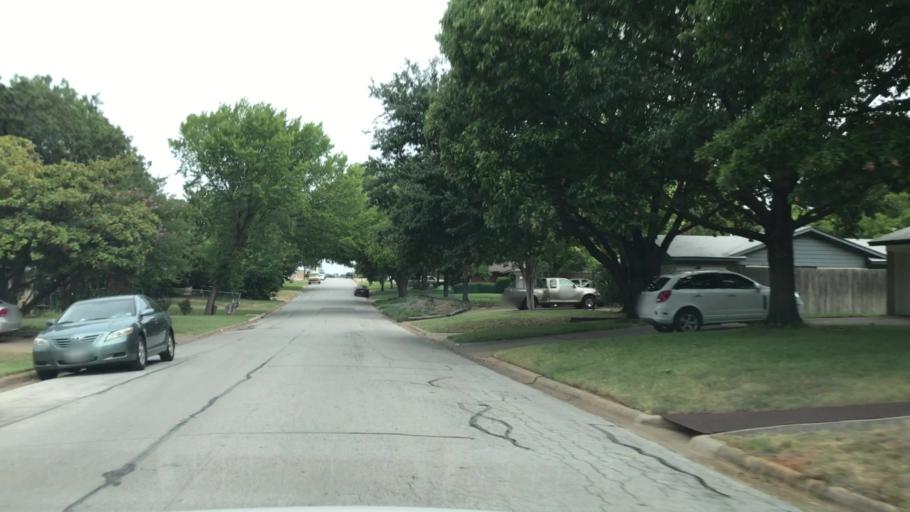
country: US
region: Texas
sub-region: Tarrant County
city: Euless
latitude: 32.8347
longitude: -97.0835
